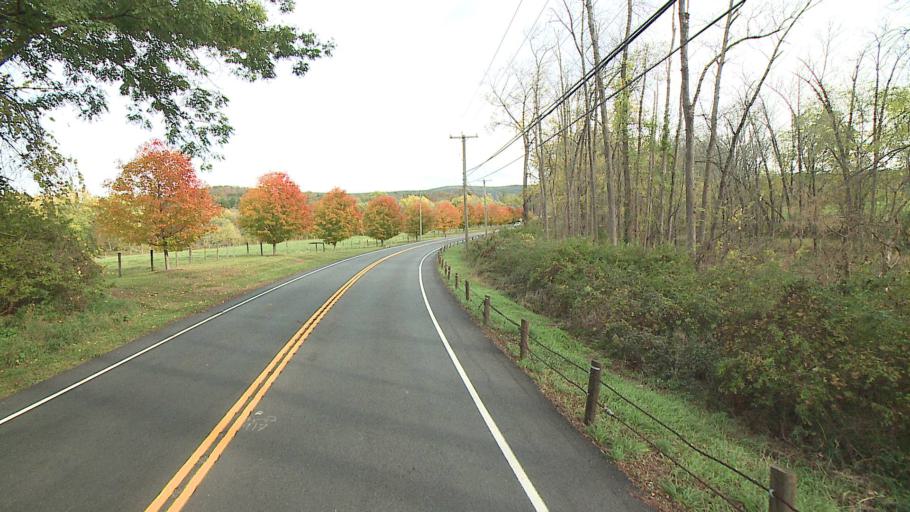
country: US
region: Connecticut
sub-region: Litchfield County
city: Canaan
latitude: 42.0069
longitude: -73.3611
